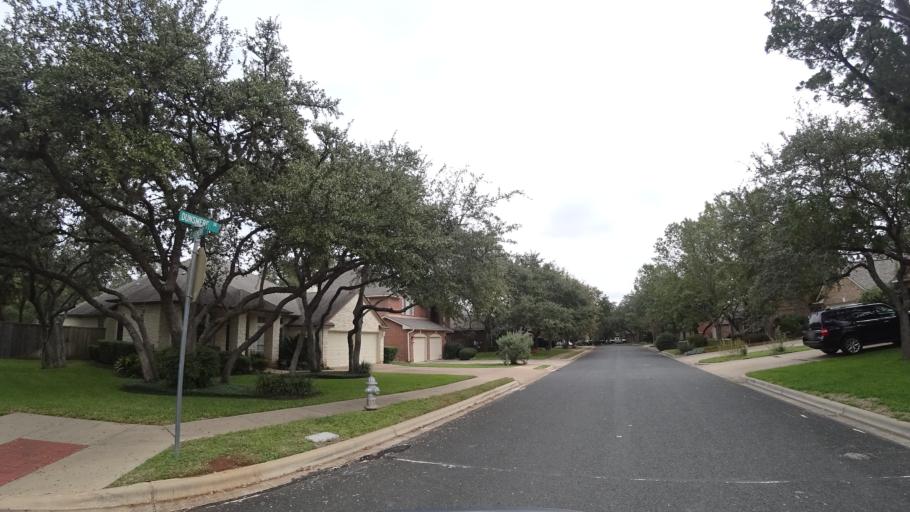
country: US
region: Texas
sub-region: Travis County
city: Shady Hollow
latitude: 30.2161
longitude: -97.8796
